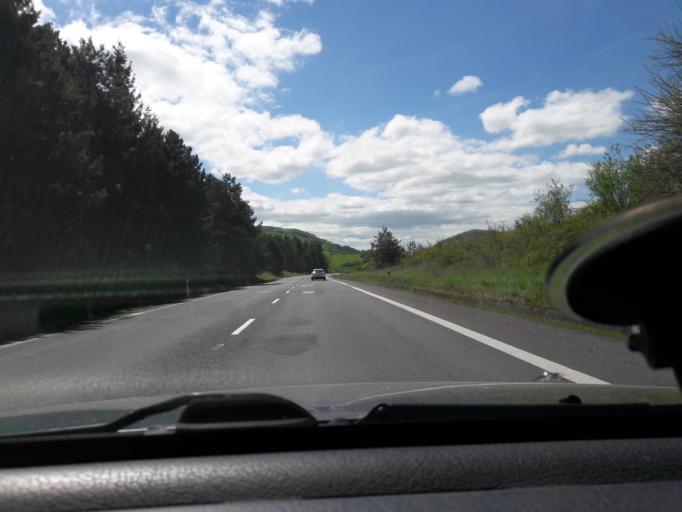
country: SK
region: Banskobystricky
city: Krupina
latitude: 48.4326
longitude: 19.0954
